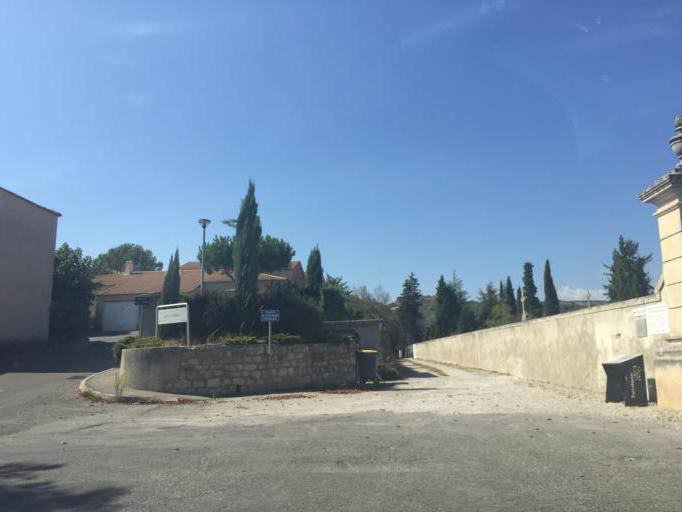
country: FR
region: Provence-Alpes-Cote d'Azur
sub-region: Departement des Alpes-de-Haute-Provence
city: Forcalquier
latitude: 43.9642
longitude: 5.7855
